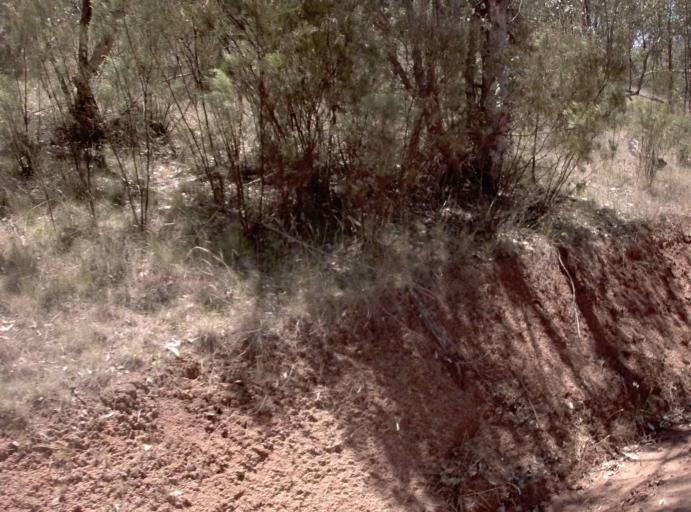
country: AU
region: New South Wales
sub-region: Snowy River
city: Jindabyne
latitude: -36.9186
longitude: 148.4186
